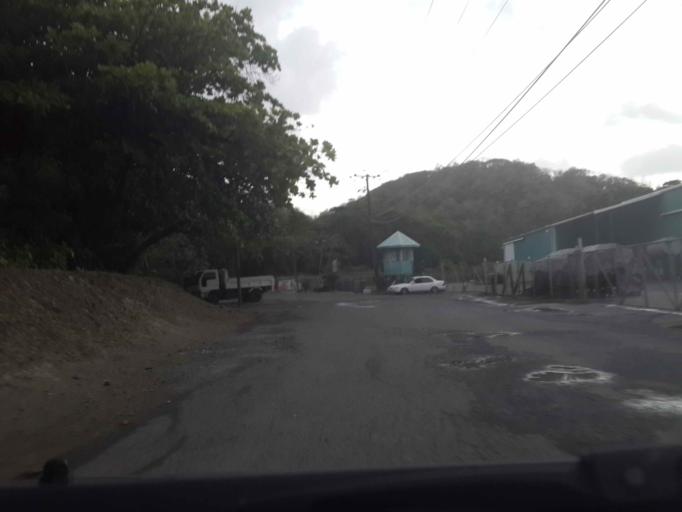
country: LC
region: Castries Quarter
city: Bisee
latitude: 14.0314
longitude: -60.9647
